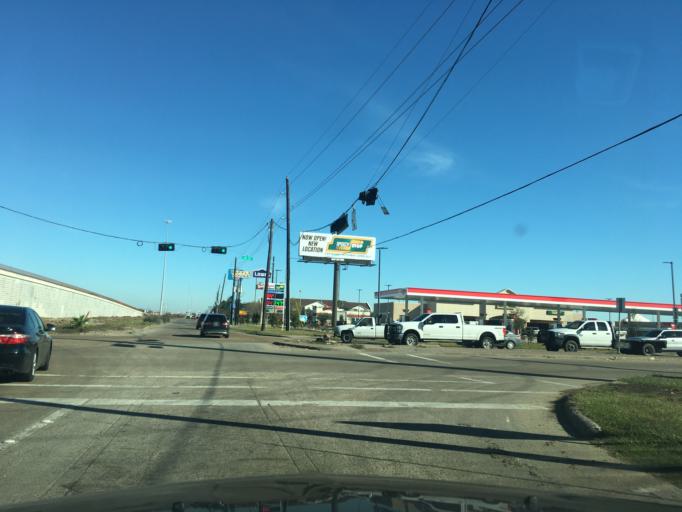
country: US
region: Texas
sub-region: Fort Bend County
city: Rosenberg
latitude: 29.5316
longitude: -95.8085
